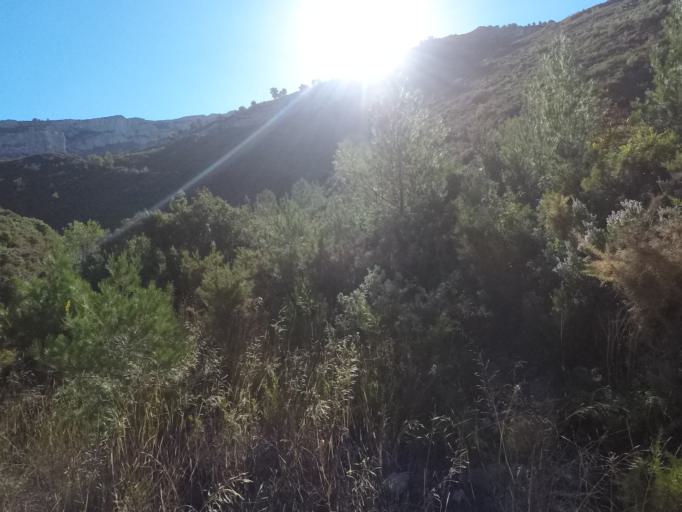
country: FR
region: Provence-Alpes-Cote d'Azur
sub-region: Departement des Bouches-du-Rhone
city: La Penne-sur-Huveaune
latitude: 43.2721
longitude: 5.4860
